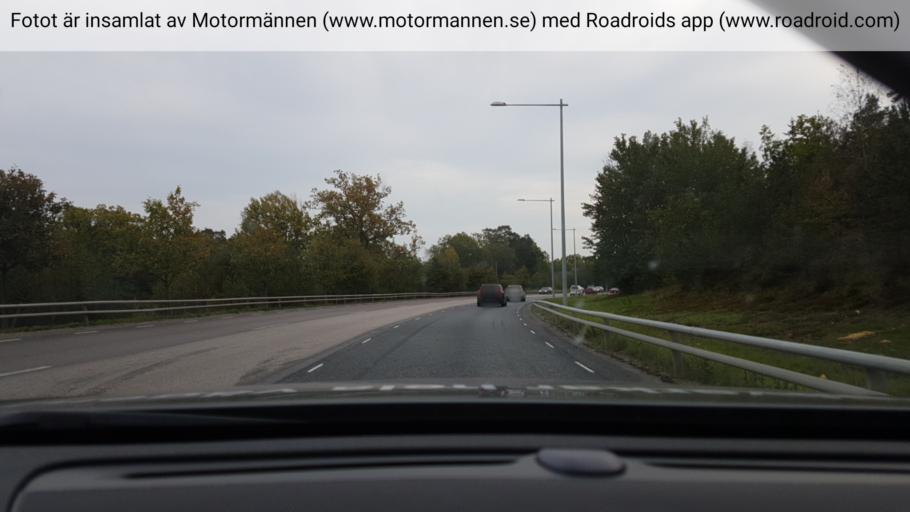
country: SE
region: Stockholm
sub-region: Nynashamns Kommun
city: Nynashamn
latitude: 58.9186
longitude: 17.9549
